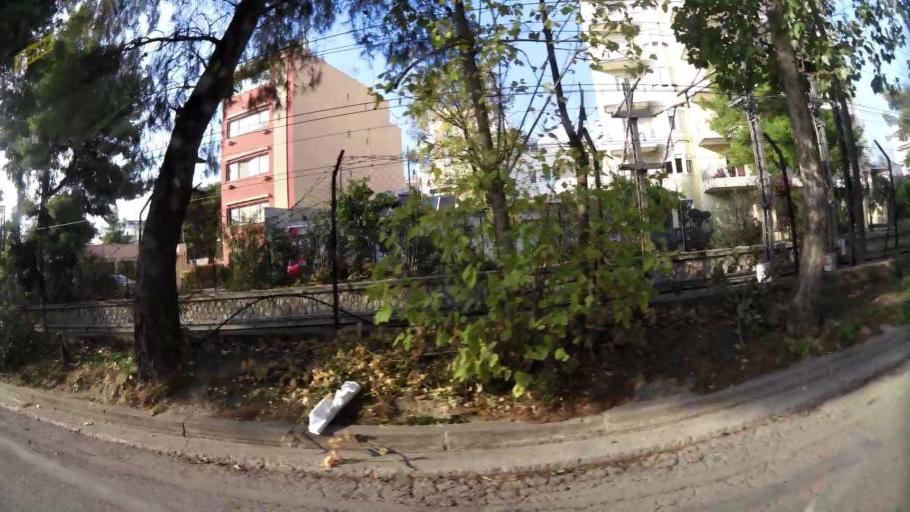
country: GR
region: Attica
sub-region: Nomarchia Anatolikis Attikis
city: Acharnes
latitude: 38.0800
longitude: 23.7408
